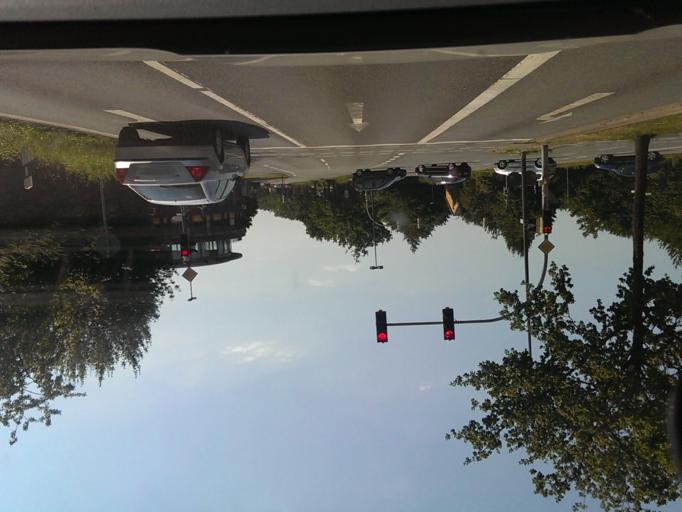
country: DE
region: Lower Saxony
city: Langenhagen
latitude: 52.4364
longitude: 9.7544
